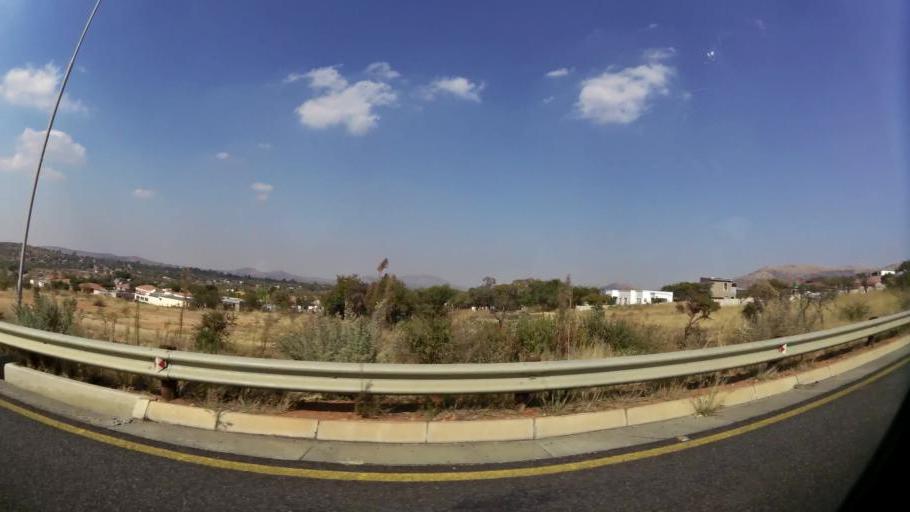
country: ZA
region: North-West
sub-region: Bojanala Platinum District Municipality
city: Rustenburg
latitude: -25.5850
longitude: 27.1301
